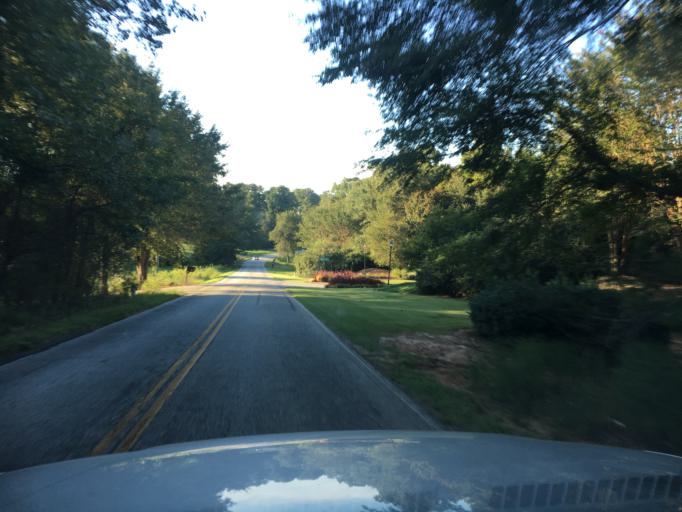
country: US
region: South Carolina
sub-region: Spartanburg County
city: Roebuck
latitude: 34.8824
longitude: -82.0481
